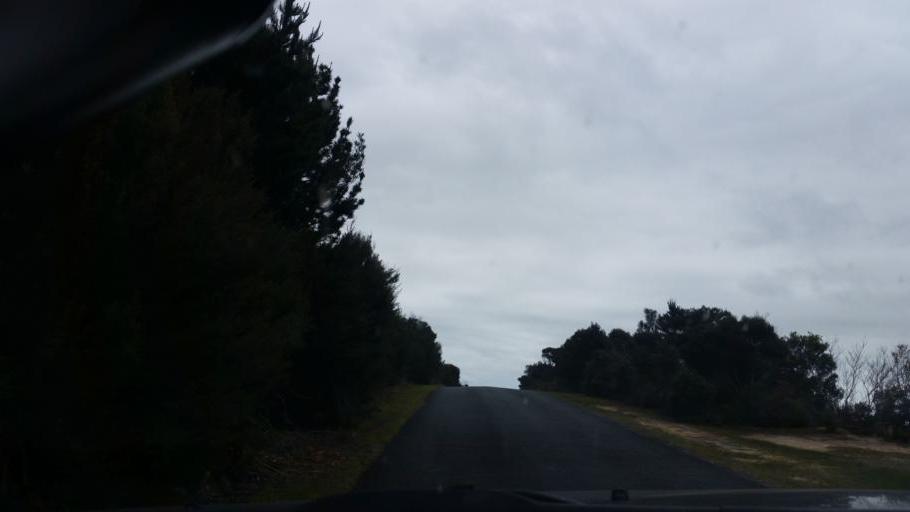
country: NZ
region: Northland
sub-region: Kaipara District
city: Dargaville
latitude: -35.8123
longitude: 173.6543
